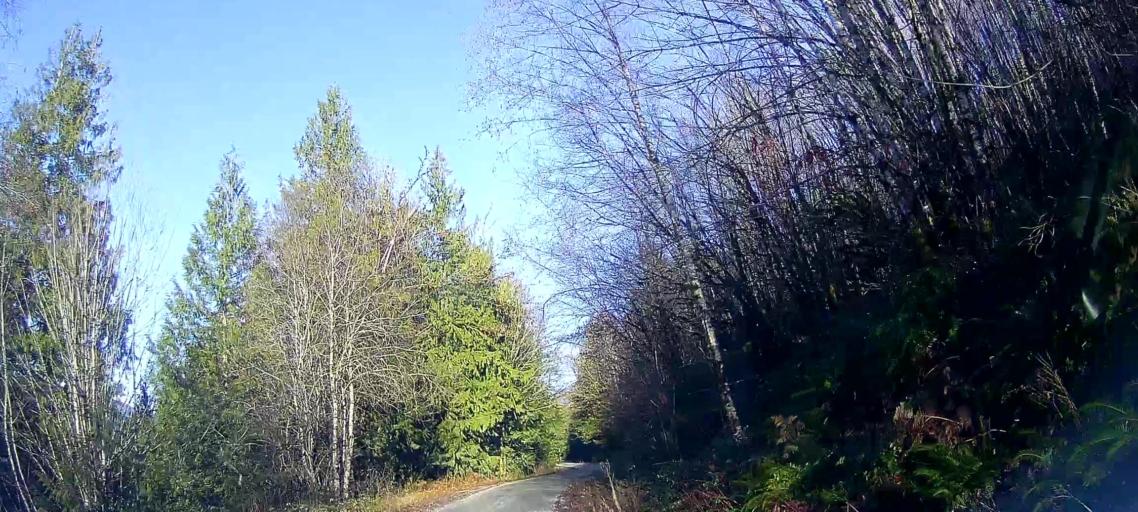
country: US
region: Washington
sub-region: Snohomish County
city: Darrington
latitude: 48.5571
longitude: -121.7252
